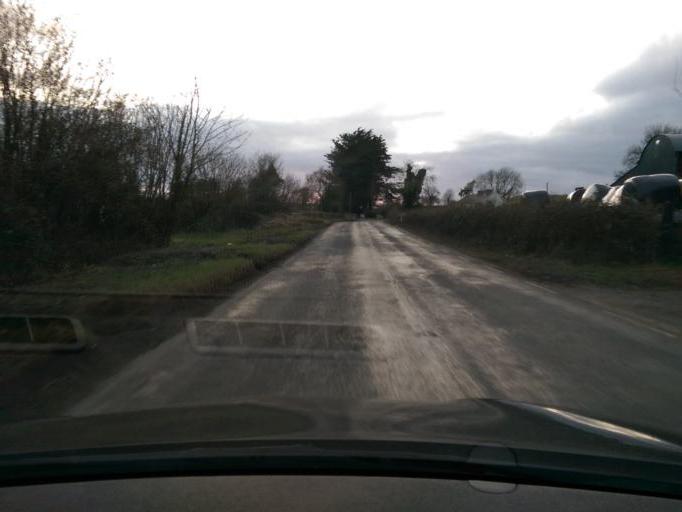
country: IE
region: Connaught
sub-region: County Galway
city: Portumna
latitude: 53.1098
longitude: -8.1176
